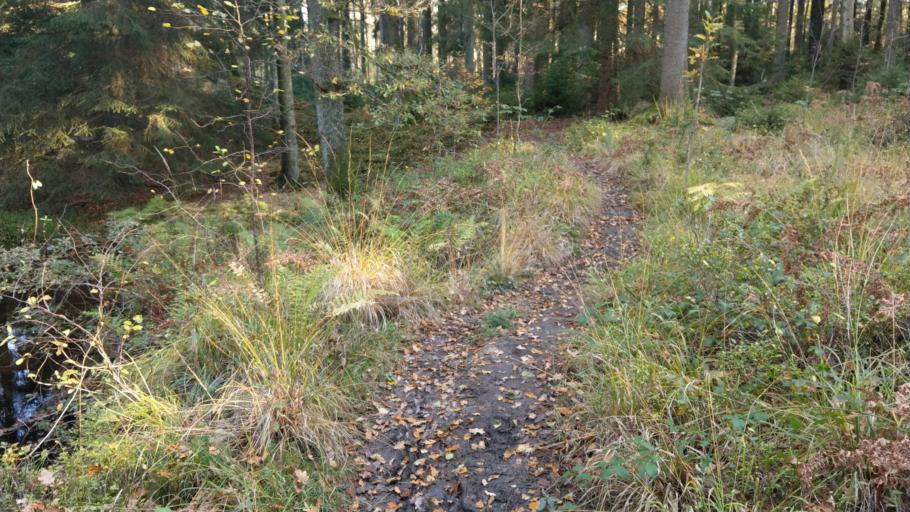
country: BE
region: Wallonia
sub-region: Province de Liege
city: Raeren
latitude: 50.6718
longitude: 6.1603
